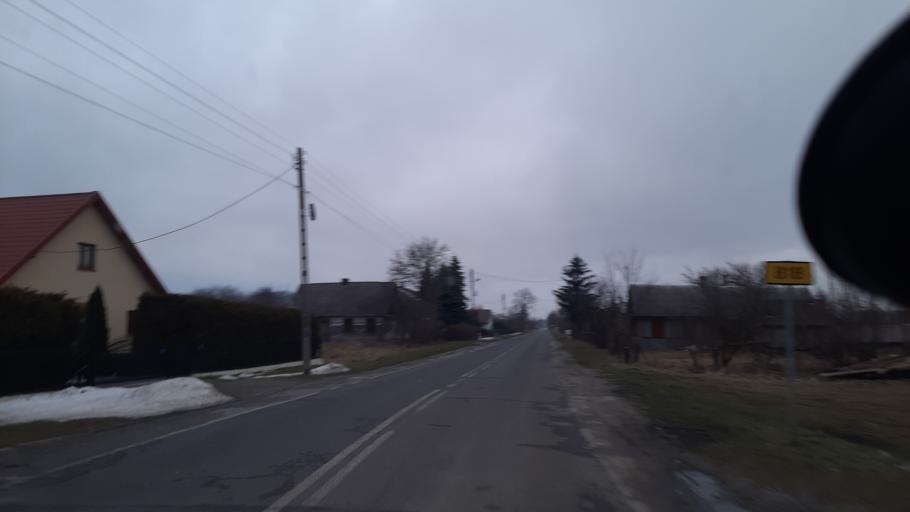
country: PL
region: Lublin Voivodeship
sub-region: Powiat parczewski
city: Sosnowica
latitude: 51.6085
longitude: 23.1247
